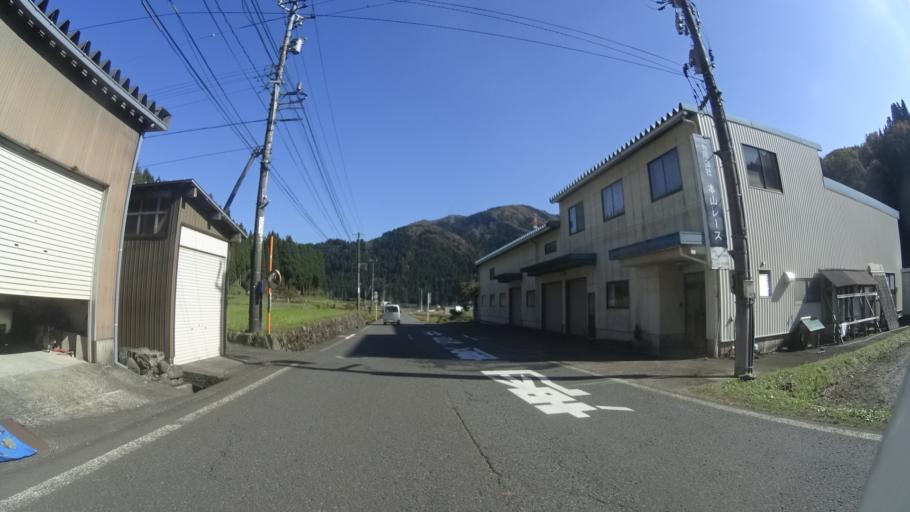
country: JP
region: Fukui
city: Ono
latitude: 35.9180
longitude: 136.3446
